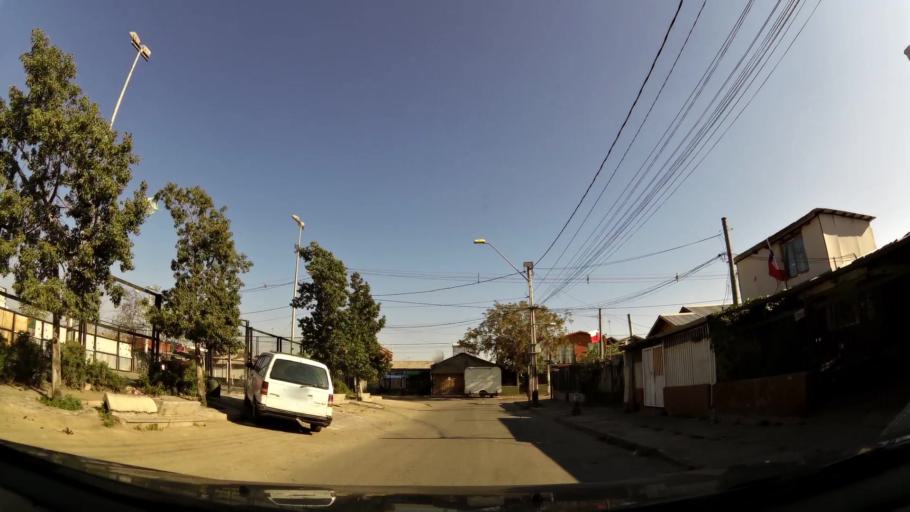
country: CL
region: Santiago Metropolitan
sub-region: Provincia de Santiago
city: La Pintana
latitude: -33.5753
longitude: -70.6551
